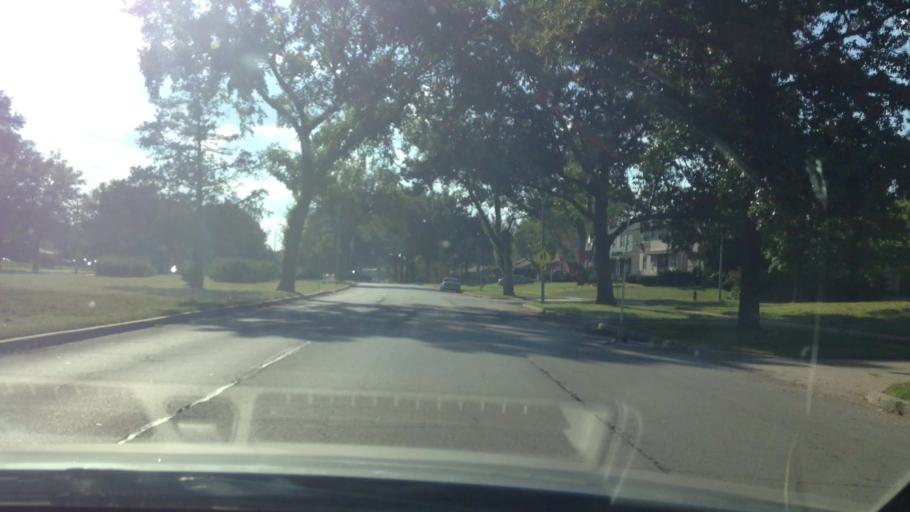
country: US
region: Kansas
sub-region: Johnson County
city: Mission Hills
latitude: 39.0080
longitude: -94.5510
